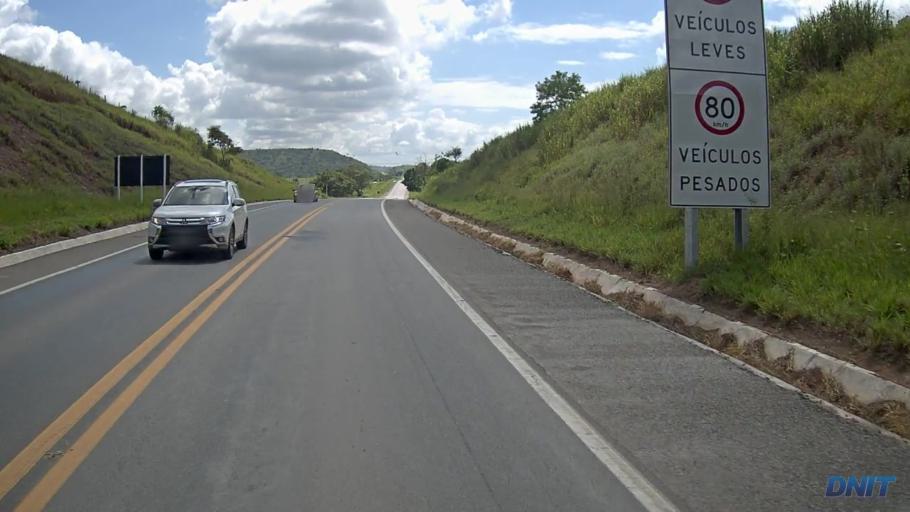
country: BR
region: Minas Gerais
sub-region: Governador Valadares
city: Governador Valadares
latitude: -19.0116
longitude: -42.1387
